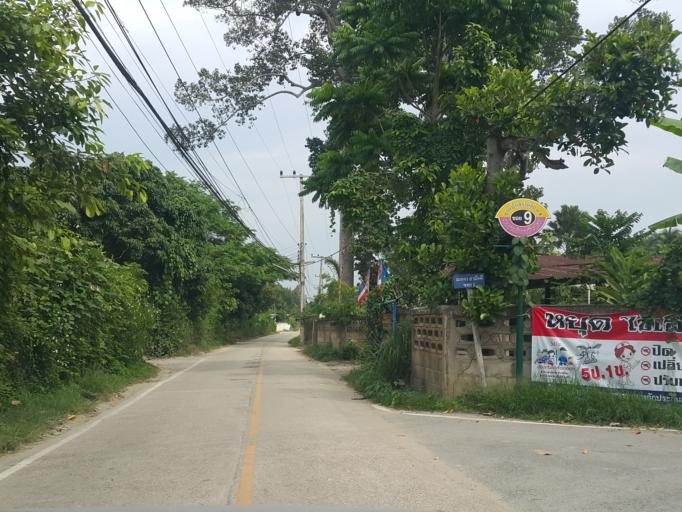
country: TH
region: Chiang Mai
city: San Sai
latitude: 18.8035
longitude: 99.0738
